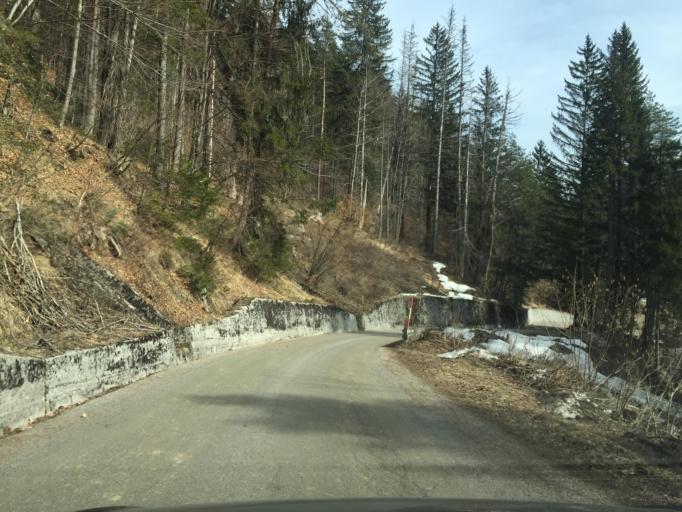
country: IT
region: Friuli Venezia Giulia
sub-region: Provincia di Udine
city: Tarvisio
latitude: 46.4967
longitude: 13.6412
